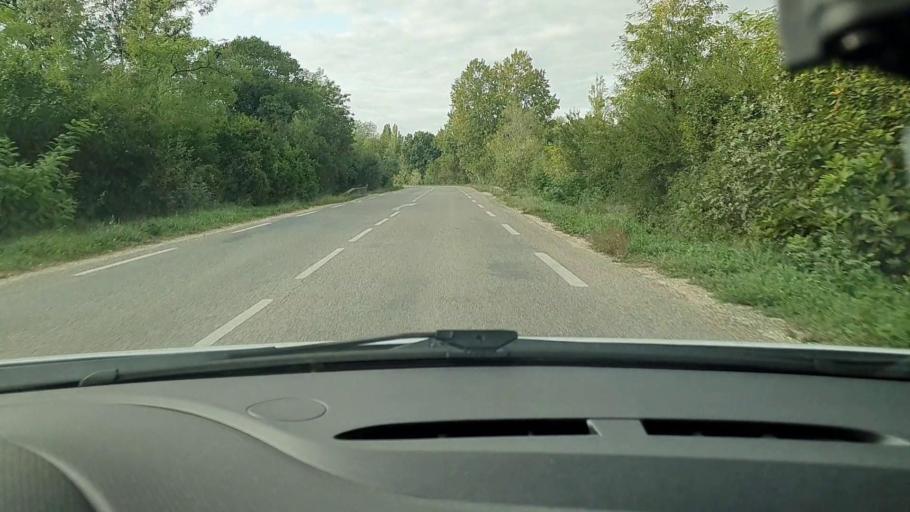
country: FR
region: Languedoc-Roussillon
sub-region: Departement du Gard
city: Saint-Ambroix
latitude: 44.2007
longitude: 4.2450
